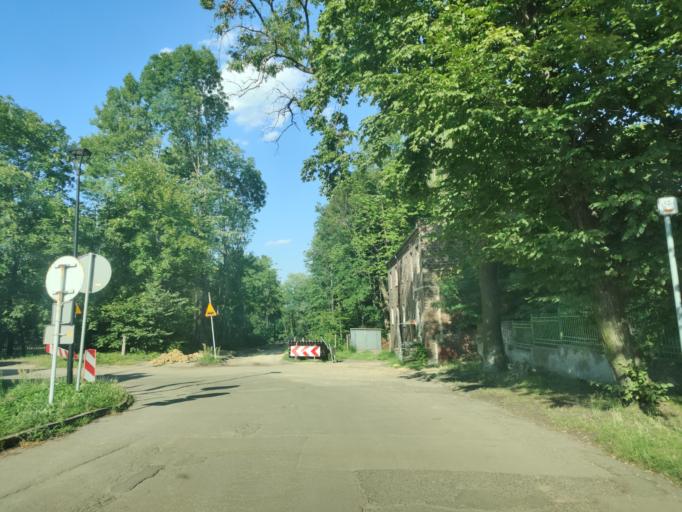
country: PL
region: Silesian Voivodeship
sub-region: Myslowice
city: Myslowice
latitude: 50.2388
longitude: 19.1430
